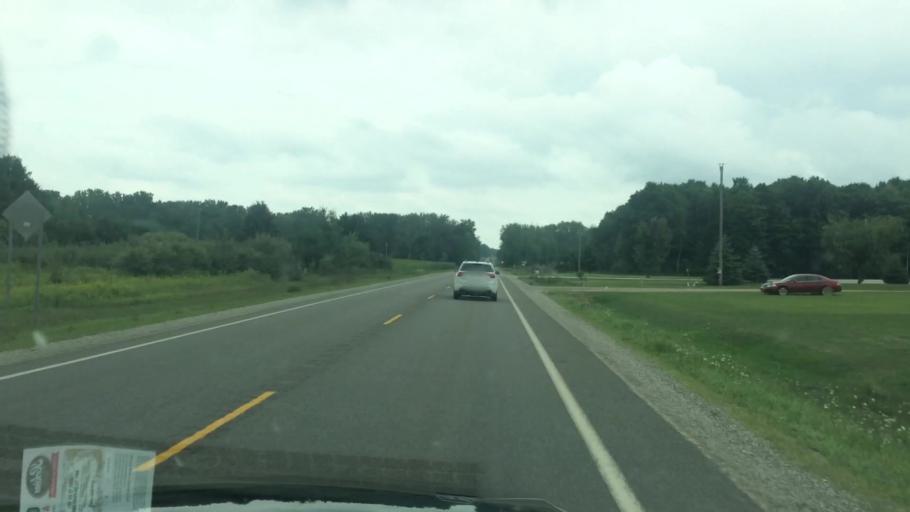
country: US
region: Michigan
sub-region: Tuscola County
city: Cass City
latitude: 43.6346
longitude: -83.0973
